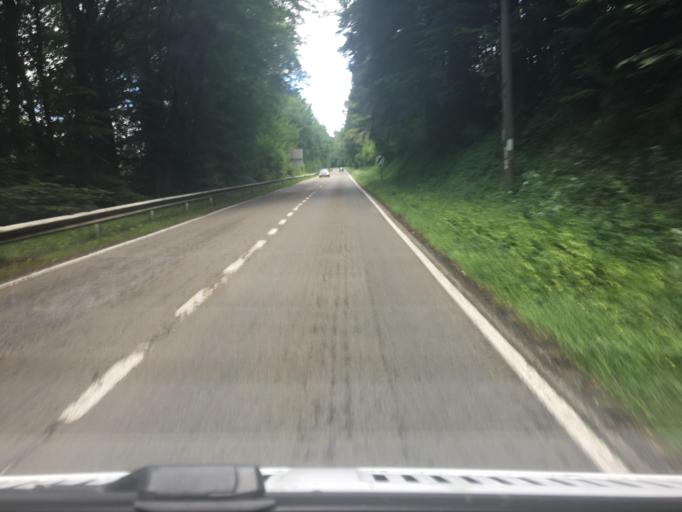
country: BE
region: Wallonia
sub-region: Province du Luxembourg
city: Florenville
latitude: 49.6355
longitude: 5.3451
